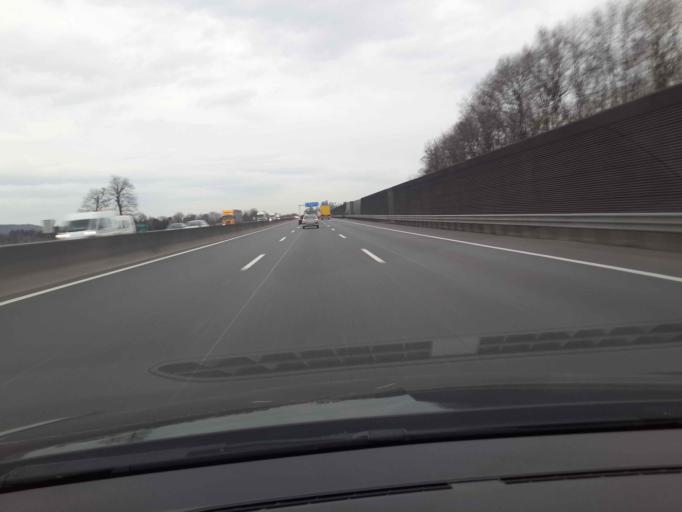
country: AT
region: Lower Austria
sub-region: Politischer Bezirk Melk
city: Neumarkt an der Ybbs
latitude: 48.1305
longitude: 15.0258
